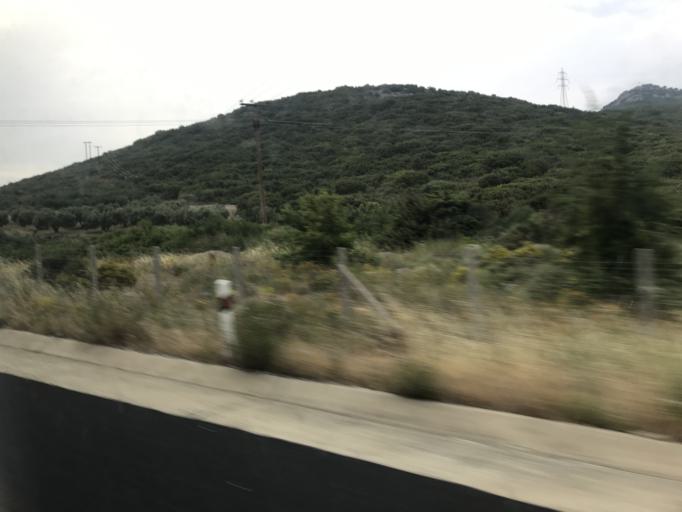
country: GR
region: East Macedonia and Thrace
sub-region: Nomos Evrou
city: Alexandroupoli
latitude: 40.8603
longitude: 25.7416
